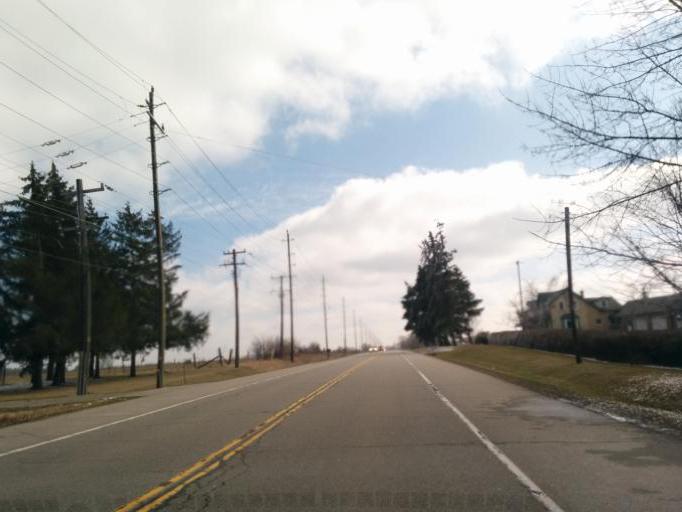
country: CA
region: Ontario
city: Waterloo
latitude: 43.5199
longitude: -80.4644
